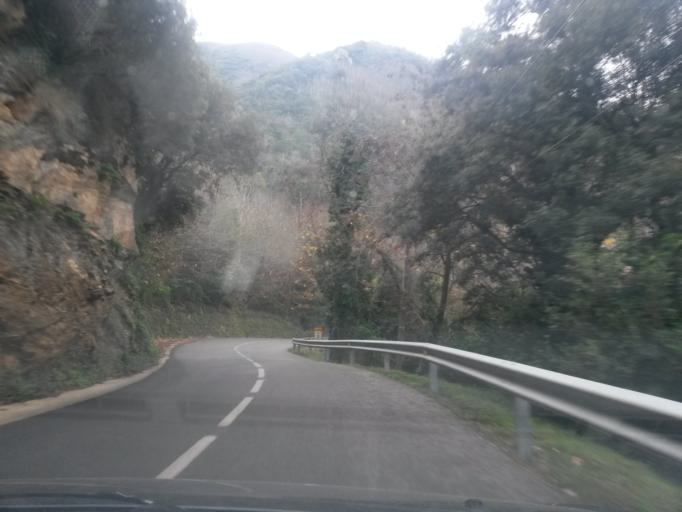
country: ES
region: Catalonia
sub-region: Provincia de Girona
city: la Cellera de Ter
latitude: 41.9500
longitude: 2.6150
